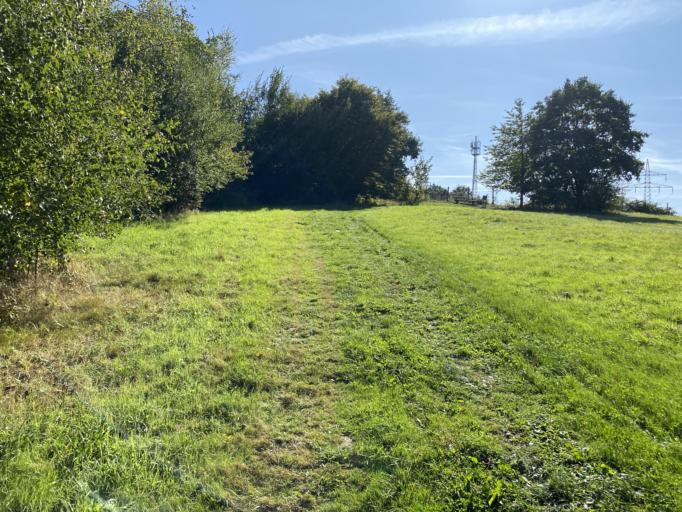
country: DE
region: North Rhine-Westphalia
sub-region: Regierungsbezirk Detmold
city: Kirchlengern
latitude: 52.1804
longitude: 8.6414
